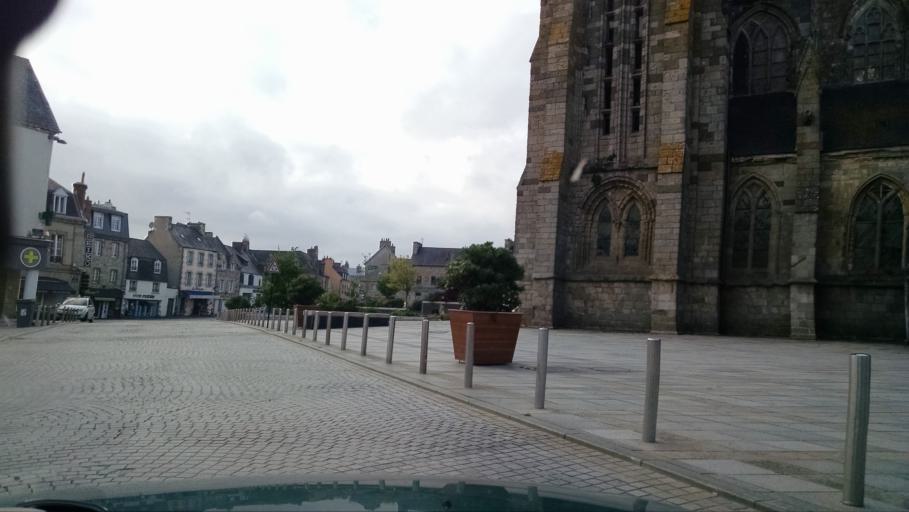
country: FR
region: Brittany
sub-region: Departement du Finistere
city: Saint-Pol-de-Leon
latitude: 48.6846
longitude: -3.9866
